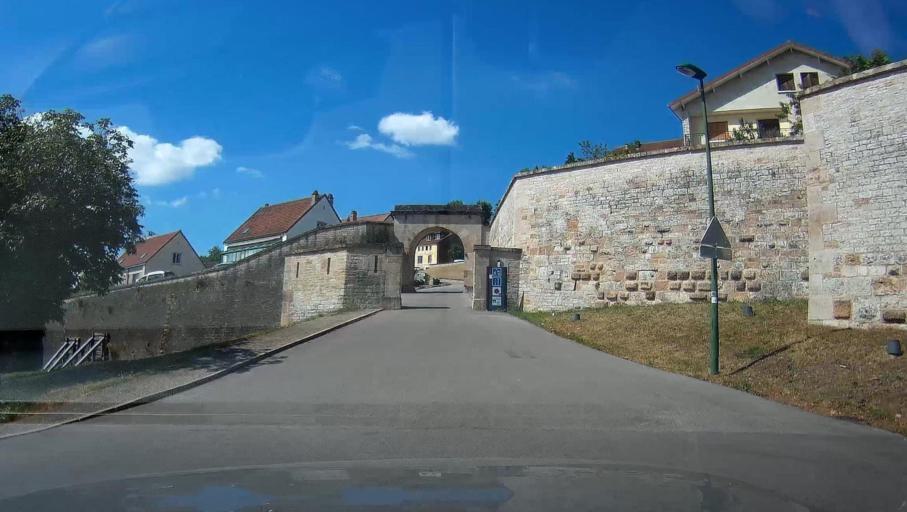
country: FR
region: Champagne-Ardenne
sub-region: Departement de la Haute-Marne
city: Langres
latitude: 47.8640
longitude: 5.3385
